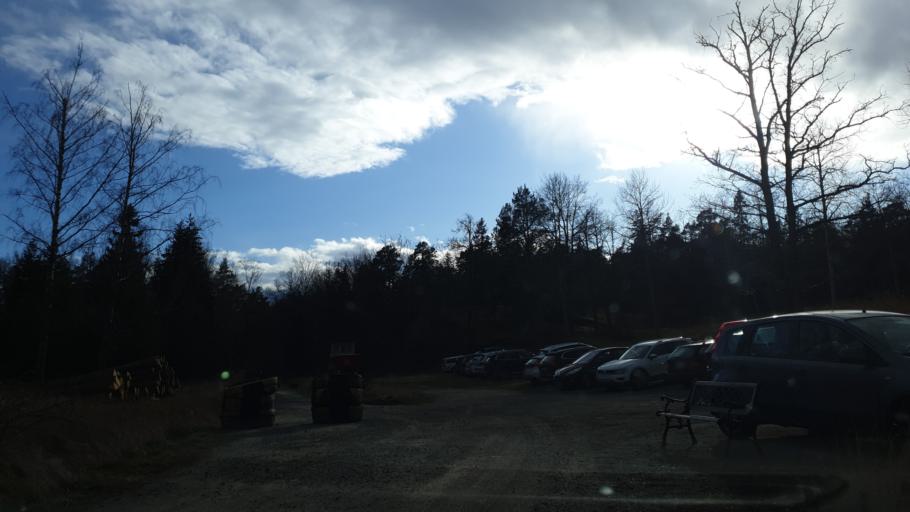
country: SE
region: Stockholm
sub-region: Varmdo Kommun
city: Holo
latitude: 59.3727
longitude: 18.6767
